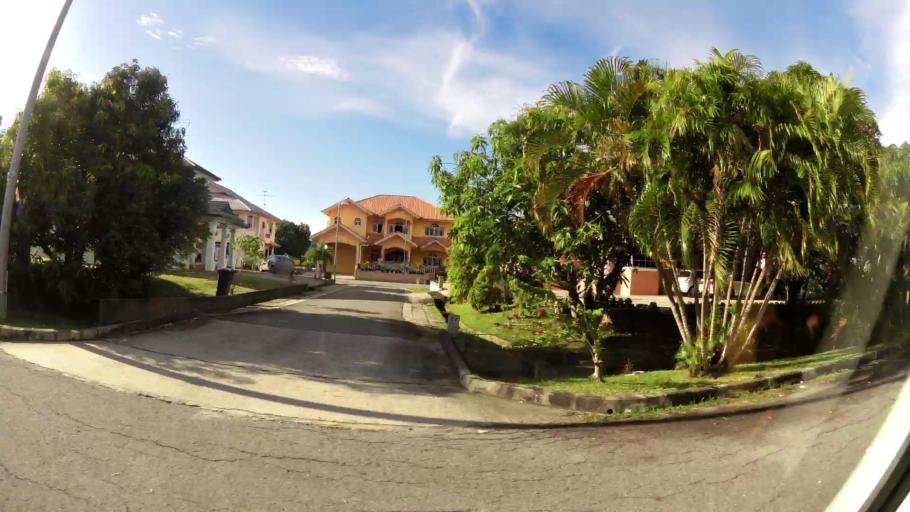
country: BN
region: Brunei and Muara
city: Bandar Seri Begawan
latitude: 4.9844
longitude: 114.9619
